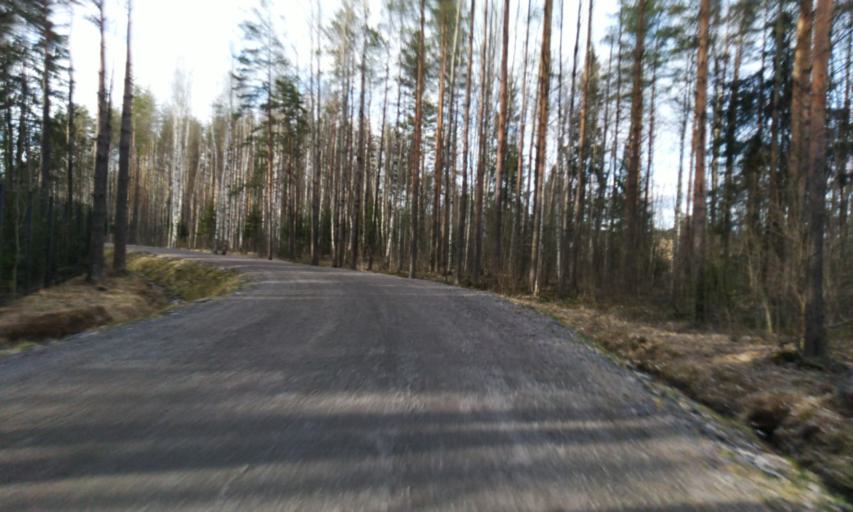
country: RU
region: Leningrad
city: Toksovo
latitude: 60.1199
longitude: 30.4784
